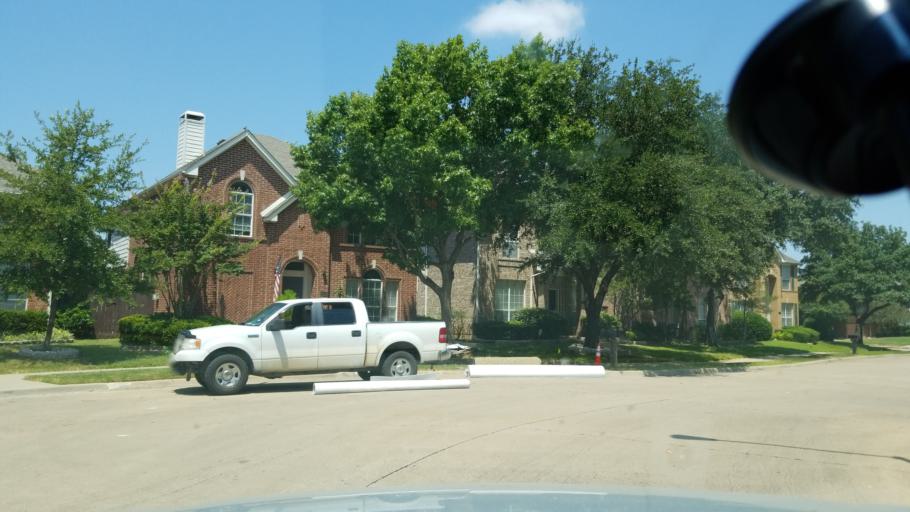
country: US
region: Texas
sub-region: Dallas County
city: Farmers Branch
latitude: 32.9260
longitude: -96.9470
